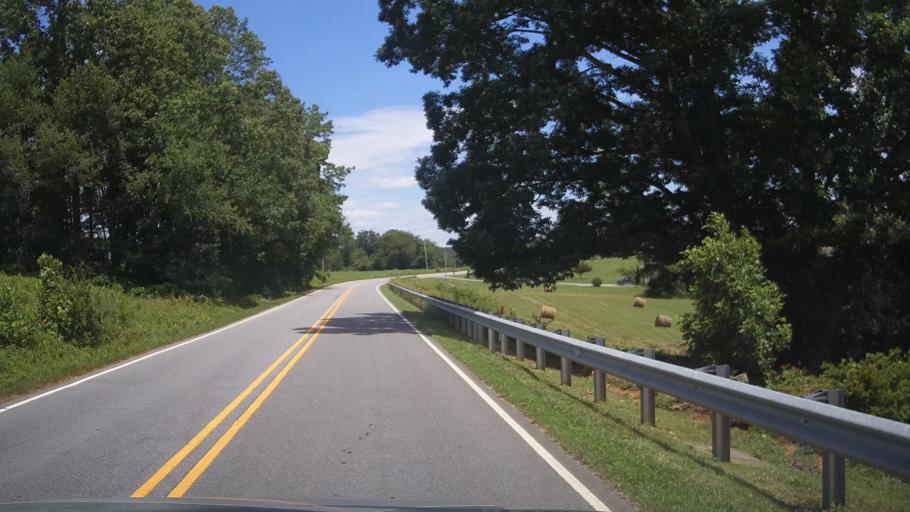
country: US
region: North Carolina
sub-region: Burke County
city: Glen Alpine
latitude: 35.6437
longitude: -81.7917
